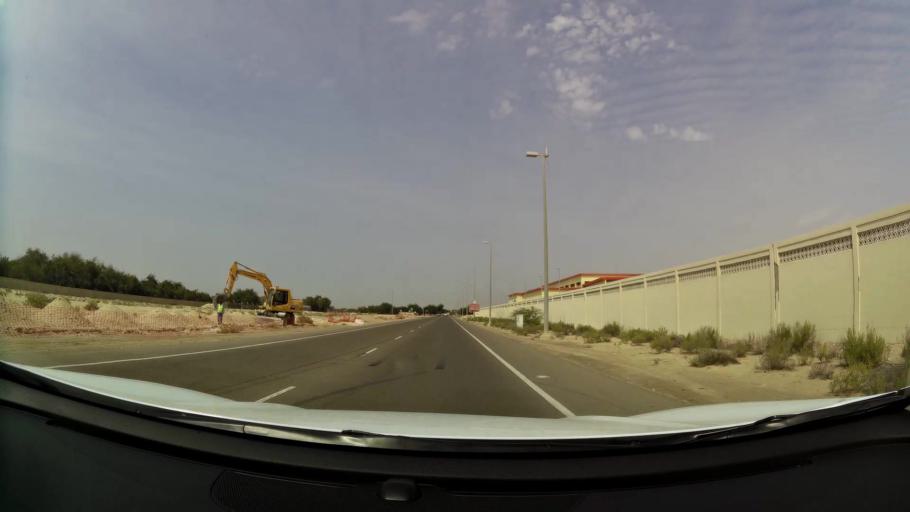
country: AE
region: Abu Dhabi
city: Abu Dhabi
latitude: 24.5627
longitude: 54.6788
